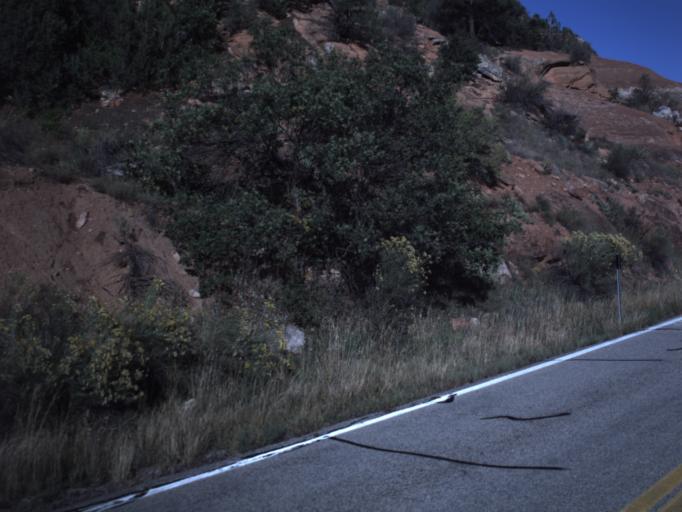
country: US
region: Utah
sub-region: San Juan County
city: Monticello
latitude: 38.3283
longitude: -109.0749
